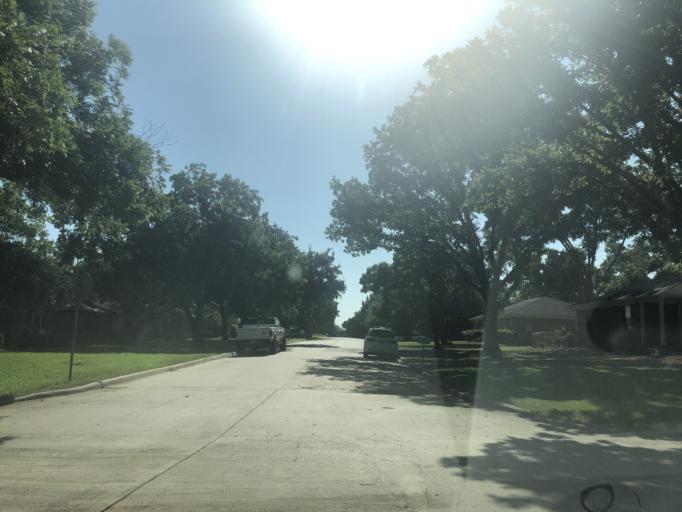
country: US
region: Texas
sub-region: Dallas County
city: Grand Prairie
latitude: 32.7623
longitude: -97.0250
